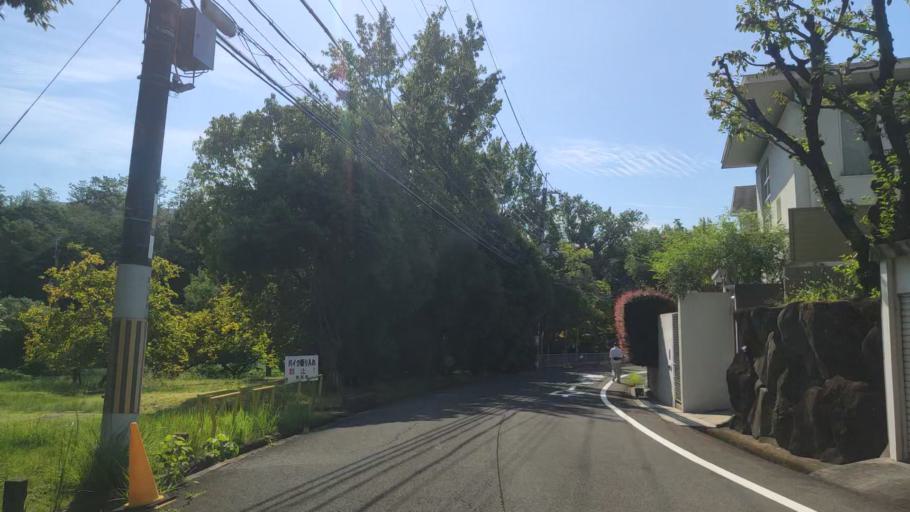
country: JP
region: Osaka
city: Mino
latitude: 34.8207
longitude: 135.5190
